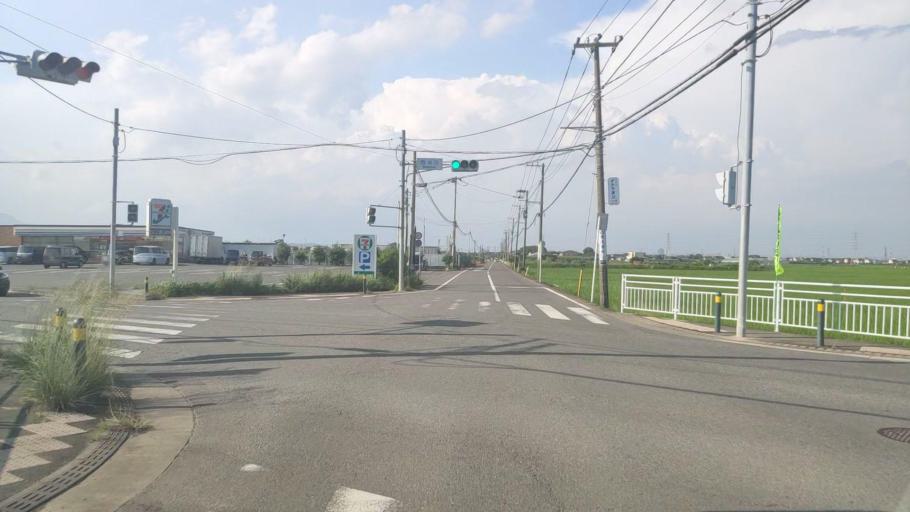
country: JP
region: Kanagawa
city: Isehara
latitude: 35.3630
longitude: 139.3274
